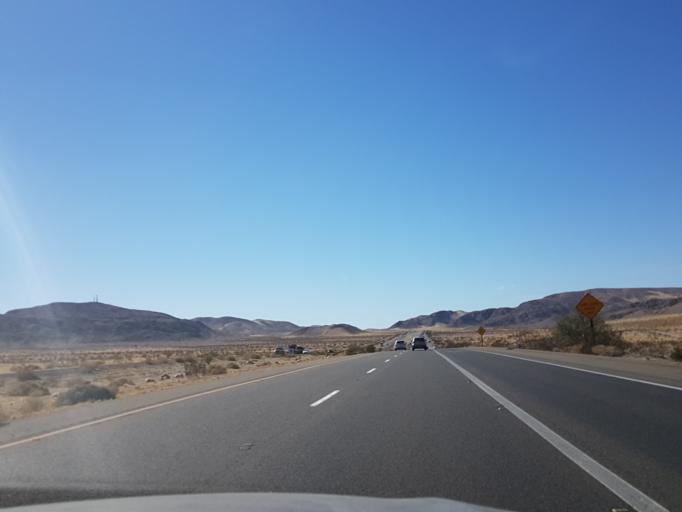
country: US
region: California
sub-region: San Bernardino County
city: Fort Irwin
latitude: 35.0875
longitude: -116.3454
